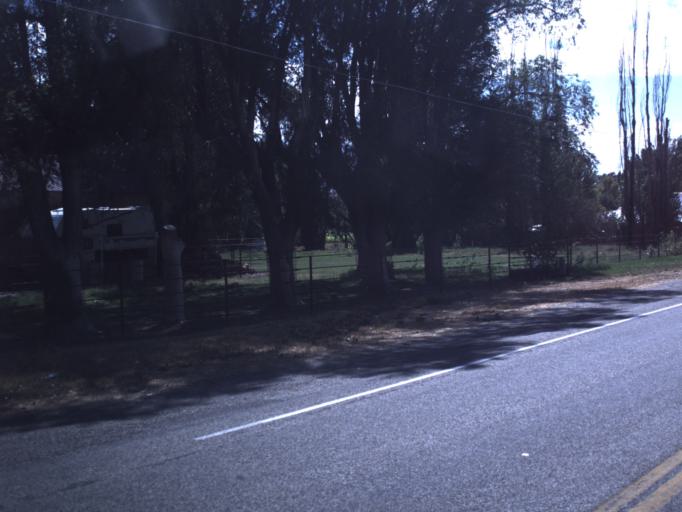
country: US
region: Utah
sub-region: Box Elder County
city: Garland
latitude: 41.7908
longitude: -112.1495
